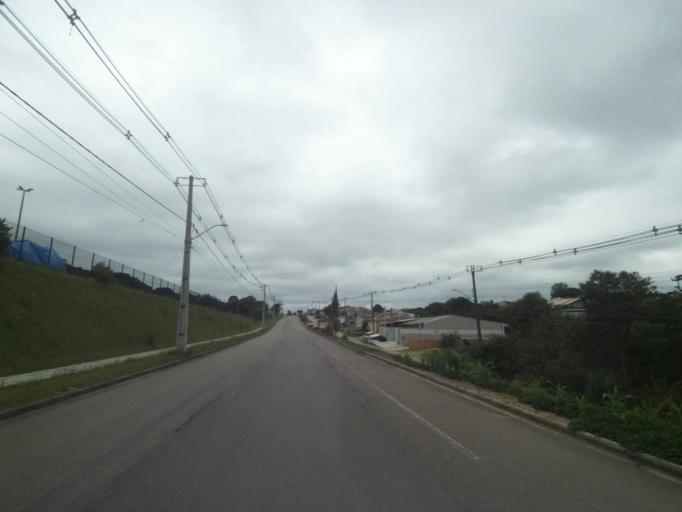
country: BR
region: Parana
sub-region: Araucaria
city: Araucaria
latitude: -25.5572
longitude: -49.3153
